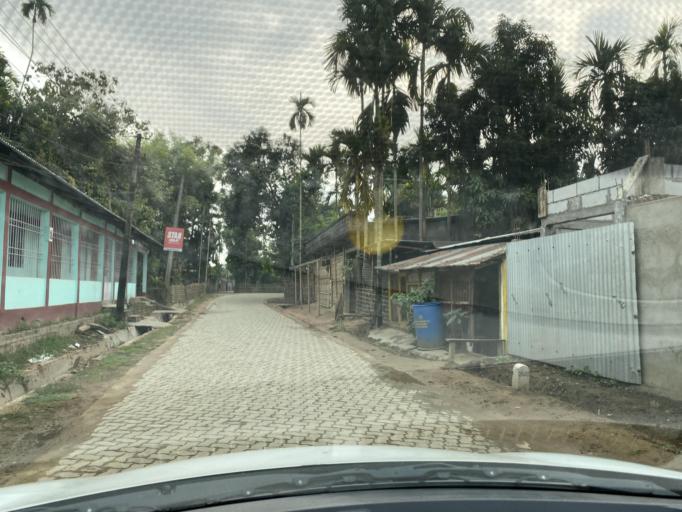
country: IN
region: Assam
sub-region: Cachar
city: Lakhipur
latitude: 24.7883
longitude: 92.9945
